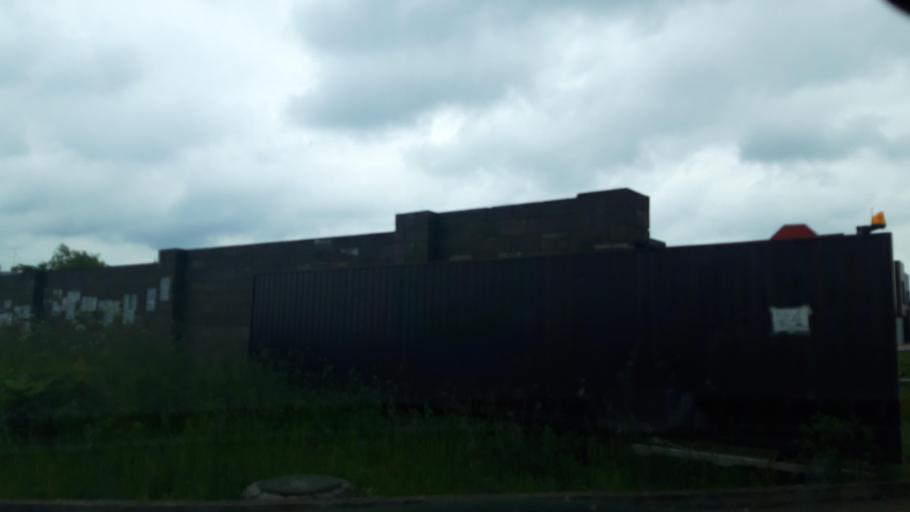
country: RU
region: Moskovskaya
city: Pavlovskaya Sloboda
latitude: 55.7776
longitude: 37.1050
